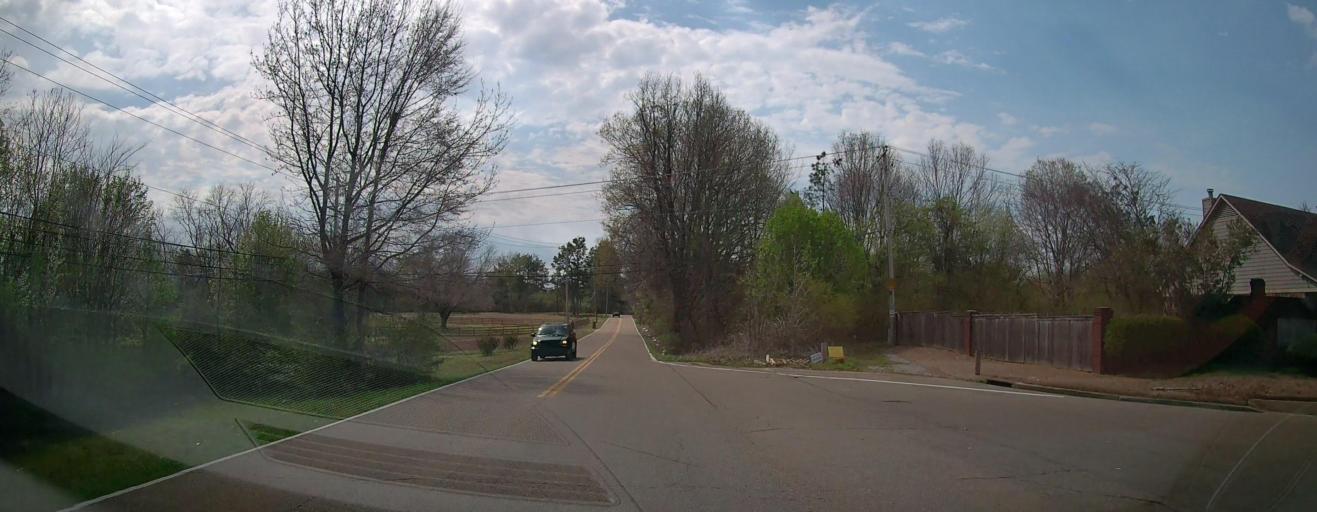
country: US
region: Mississippi
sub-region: De Soto County
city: Olive Branch
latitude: 35.0007
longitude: -89.8484
